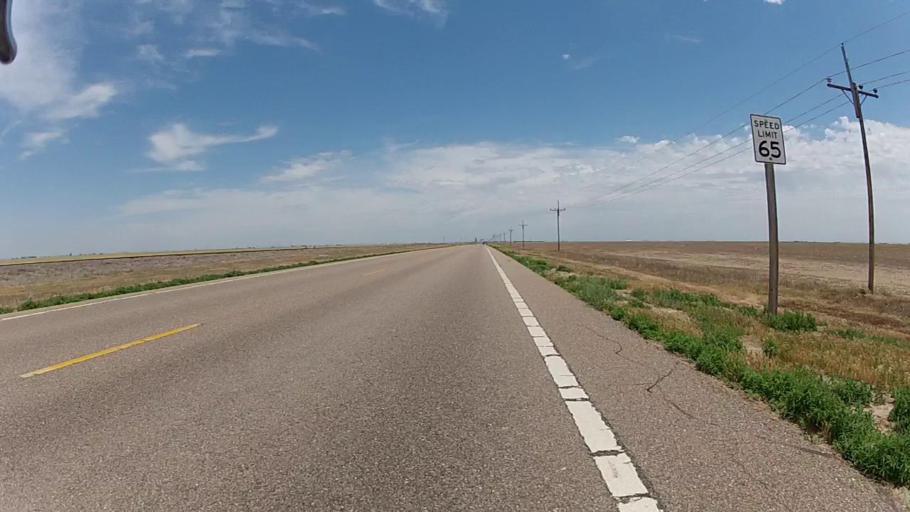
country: US
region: Kansas
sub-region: Haskell County
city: Satanta
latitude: 37.4611
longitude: -100.9234
